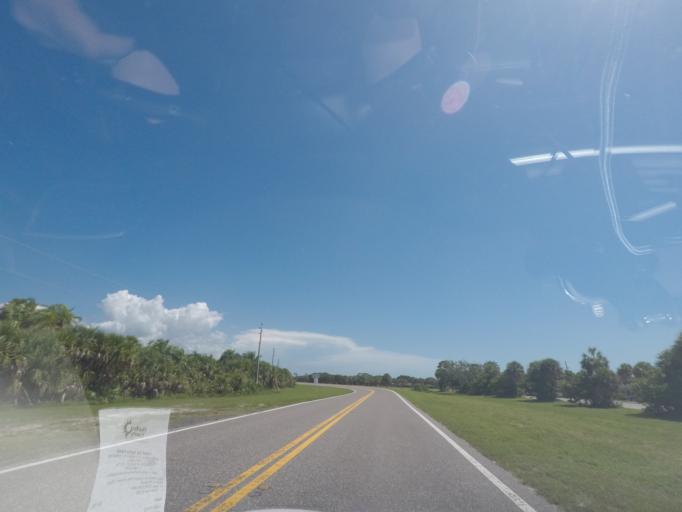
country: US
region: Florida
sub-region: Pinellas County
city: Tierra Verde
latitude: 27.6179
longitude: -82.7348
